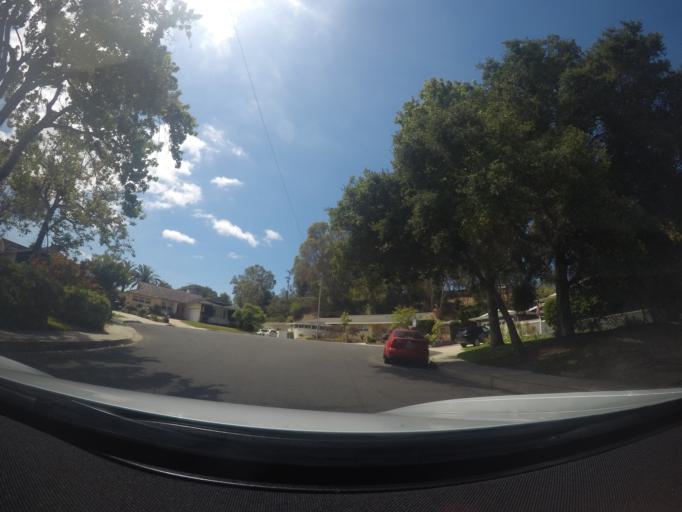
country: US
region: California
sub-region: Los Angeles County
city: Rolling Hills Estates
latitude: 33.8049
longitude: -118.3676
